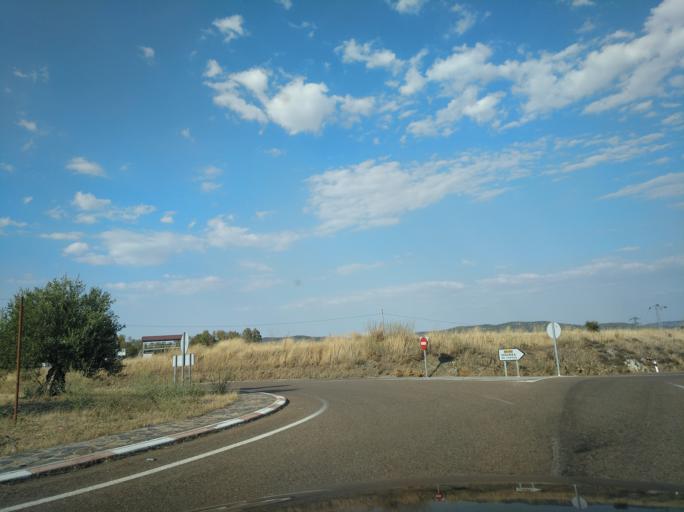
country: ES
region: Extremadura
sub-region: Provincia de Badajoz
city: Alconchel
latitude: 38.5093
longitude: -7.0700
